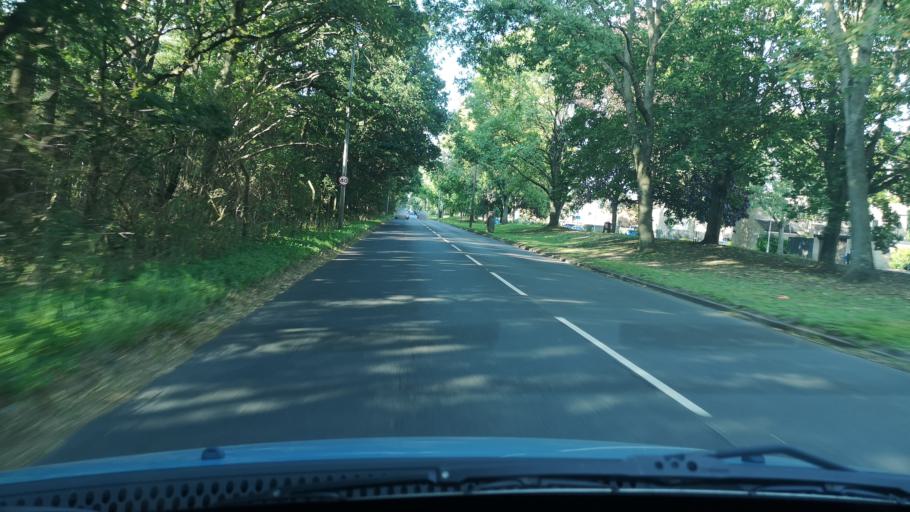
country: GB
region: England
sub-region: North Lincolnshire
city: Scunthorpe
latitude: 53.5780
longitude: -0.6836
